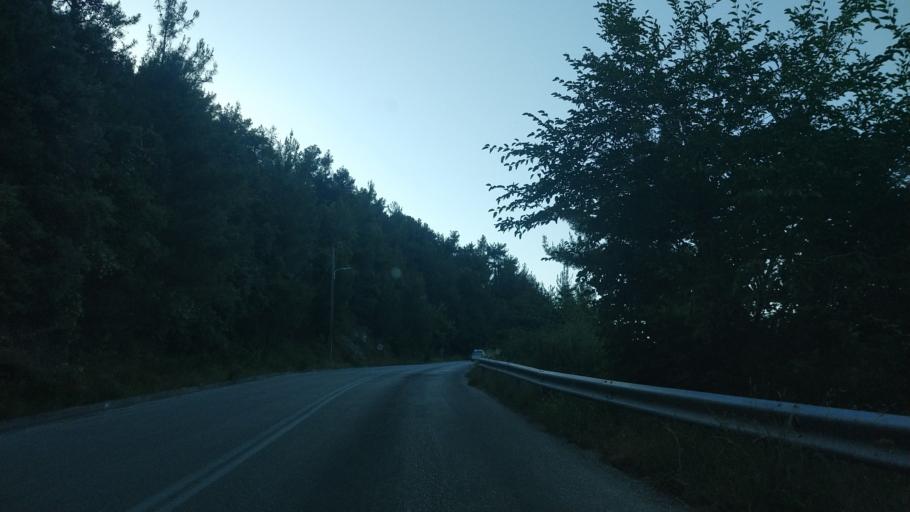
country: GR
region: East Macedonia and Thrace
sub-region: Nomos Kavalas
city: Potamia
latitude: 40.7273
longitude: 24.7331
